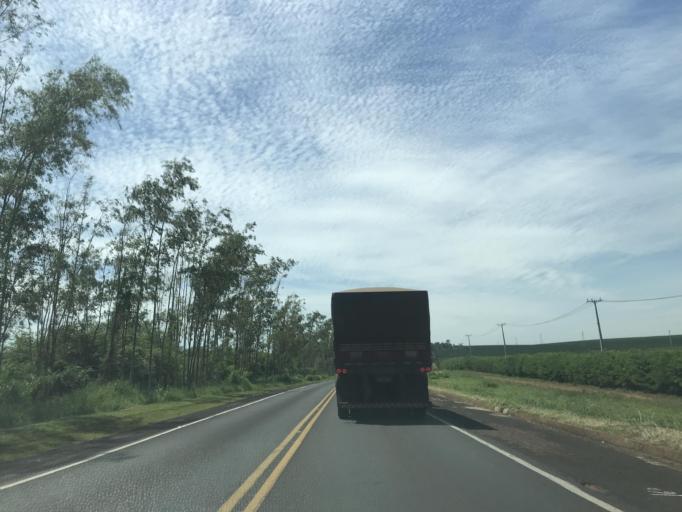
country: BR
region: Parana
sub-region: Paranavai
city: Nova Aurora
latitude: -22.9575
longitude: -52.6558
